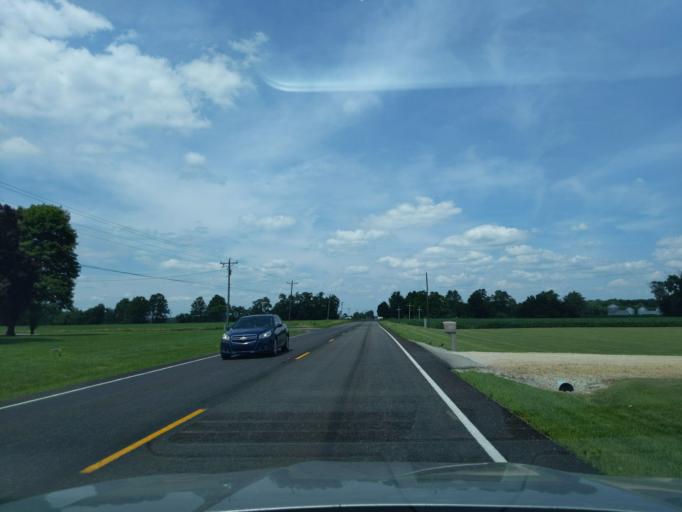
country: US
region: Indiana
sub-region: Ripley County
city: Osgood
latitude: 39.2185
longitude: -85.3340
